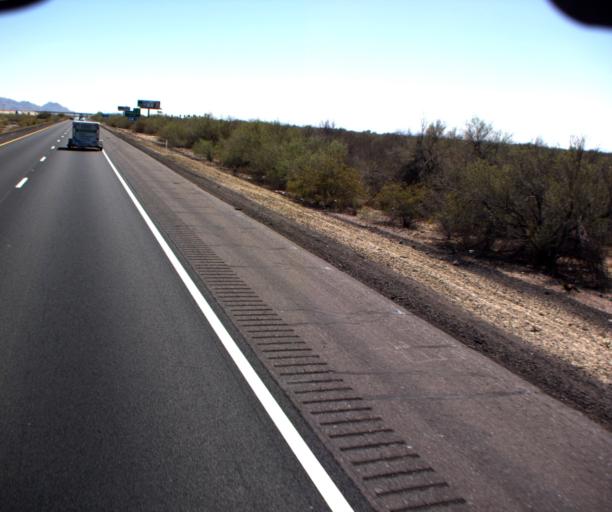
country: US
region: Arizona
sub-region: La Paz County
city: Salome
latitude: 33.6327
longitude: -113.7809
